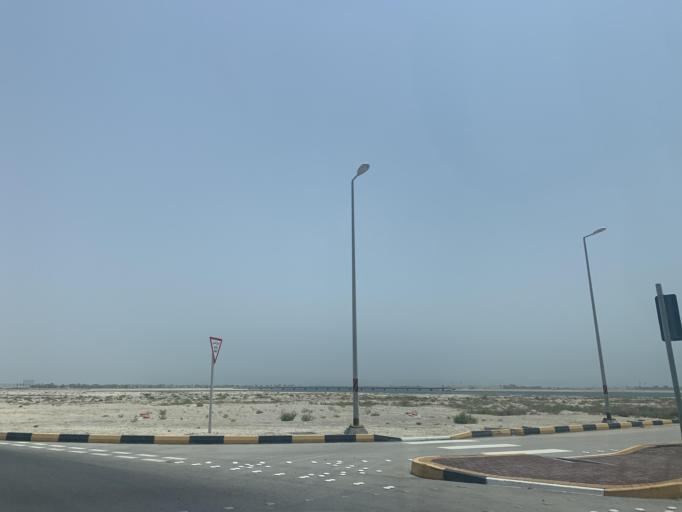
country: BH
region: Central Governorate
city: Dar Kulayb
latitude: 25.8387
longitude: 50.5923
